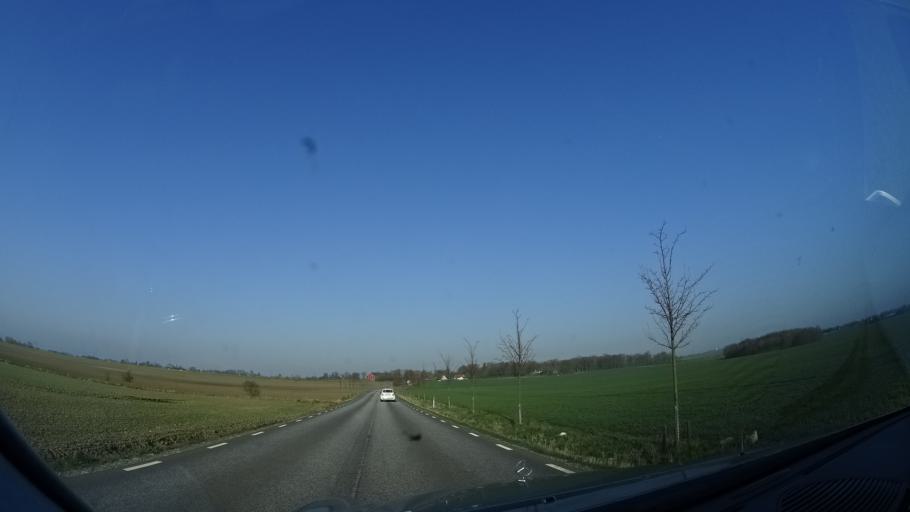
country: SE
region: Skane
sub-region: Eslovs Kommun
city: Eslov
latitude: 55.8074
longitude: 13.3433
